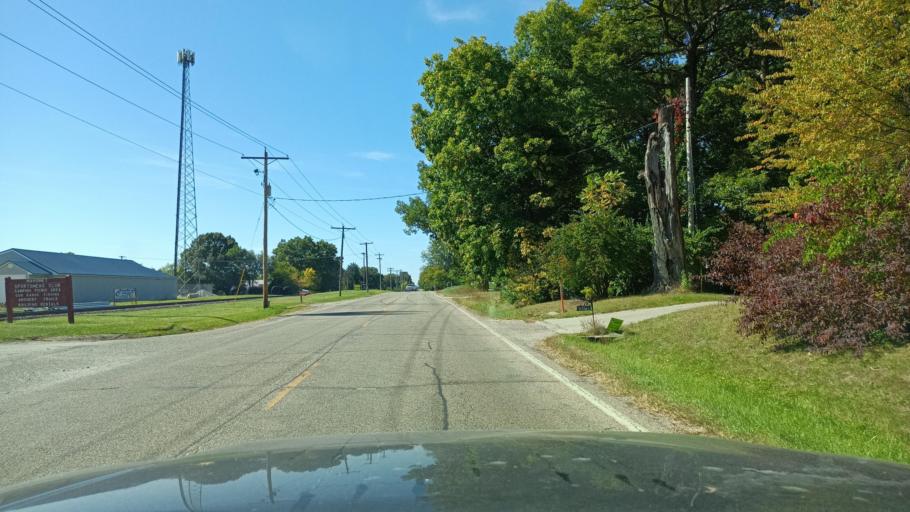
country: US
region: Illinois
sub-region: Champaign County
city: Mahomet
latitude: 40.1932
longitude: -88.4162
